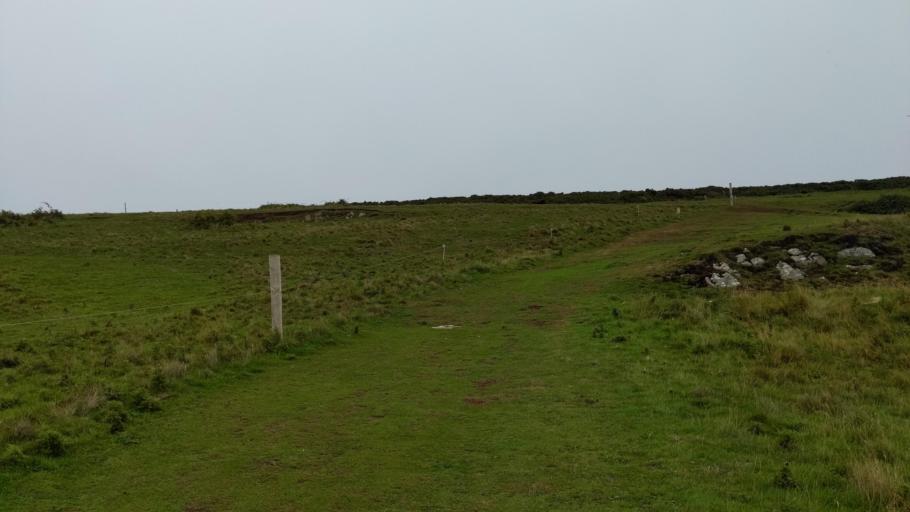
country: IE
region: Leinster
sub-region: Lu
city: Clogherhead
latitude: 53.7922
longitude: -6.2223
